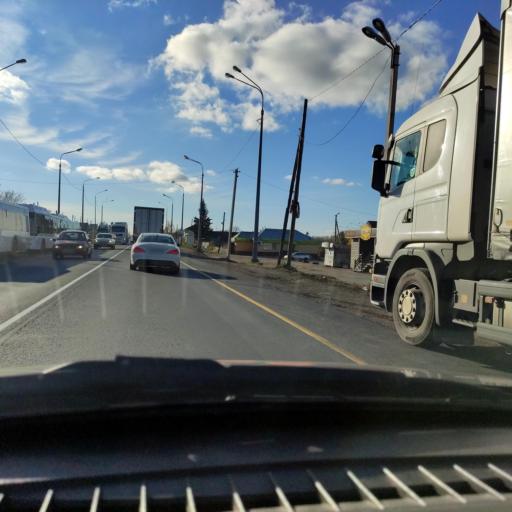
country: RU
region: Samara
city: Zhigulevsk
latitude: 53.3246
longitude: 49.4060
